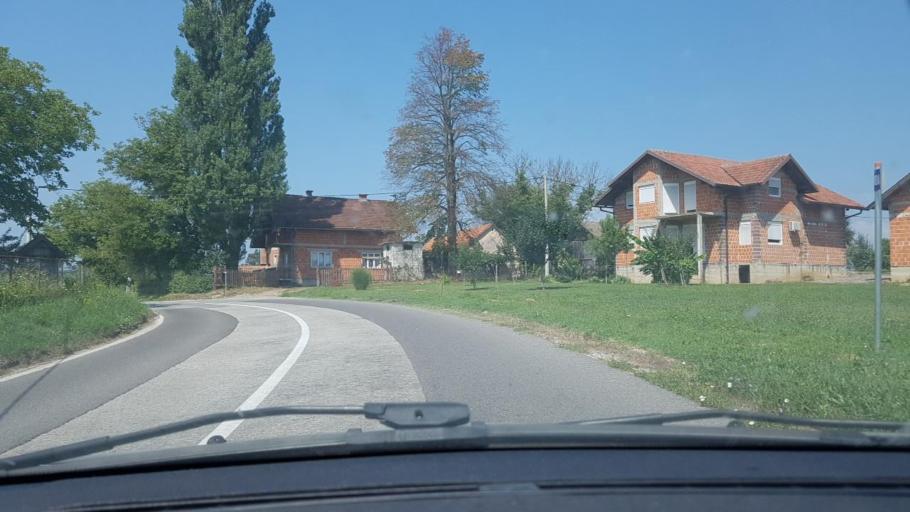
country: BA
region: Federation of Bosnia and Herzegovina
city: Velika Kladusa
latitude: 45.2137
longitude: 15.7380
